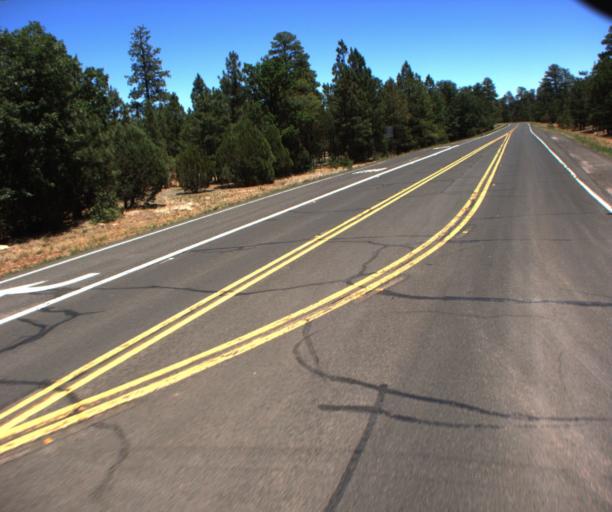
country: US
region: Arizona
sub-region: Gila County
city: Star Valley
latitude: 34.6273
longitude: -111.1267
